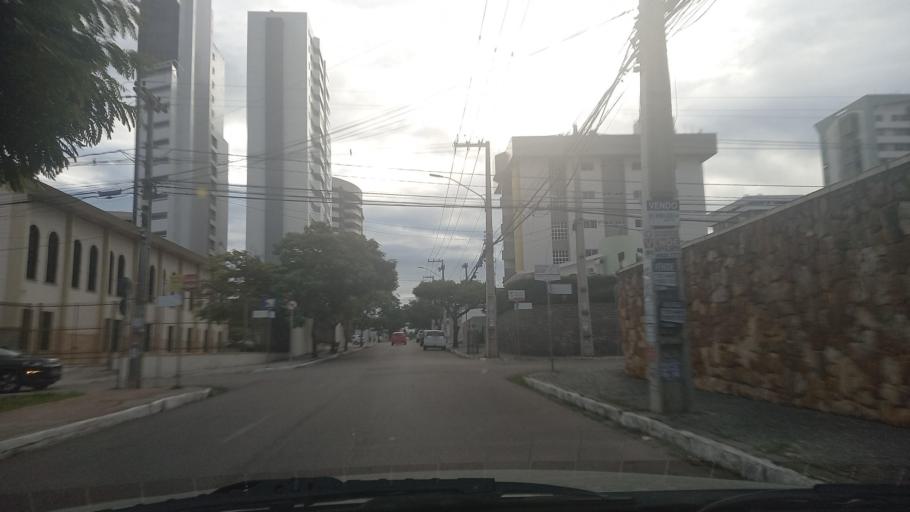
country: BR
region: Pernambuco
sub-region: Caruaru
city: Caruaru
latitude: -8.2703
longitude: -35.9725
